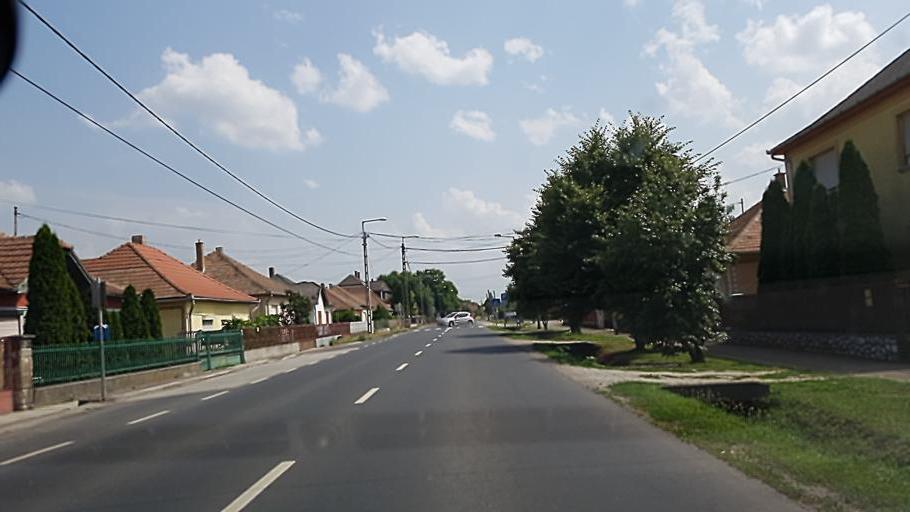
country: HU
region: Heves
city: Besenyotelek
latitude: 47.7073
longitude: 20.4261
